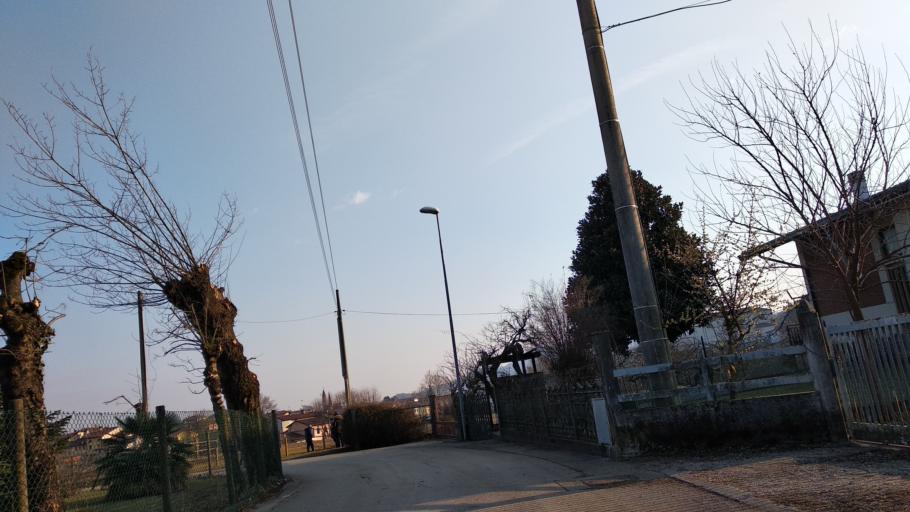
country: IT
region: Veneto
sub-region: Provincia di Vicenza
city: San Vito di Leguzzano
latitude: 45.6843
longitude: 11.3716
